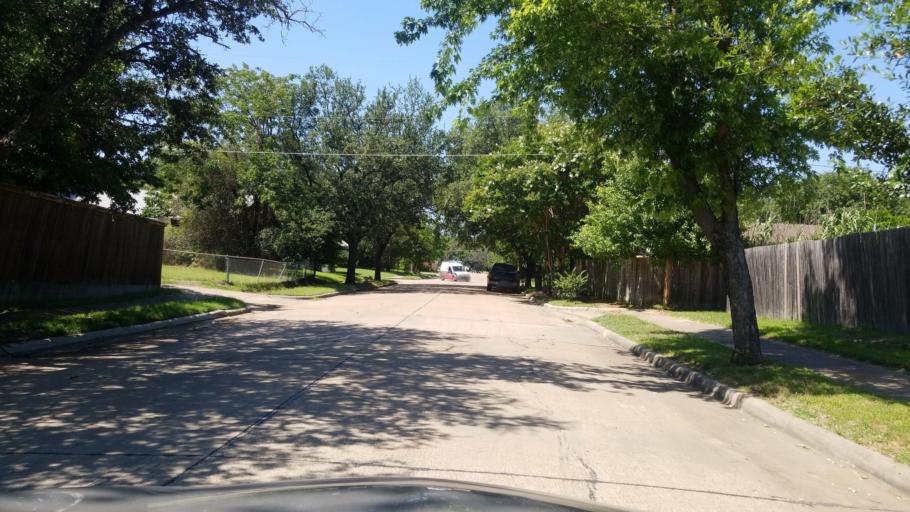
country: US
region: Texas
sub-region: Dallas County
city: Grand Prairie
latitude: 32.6925
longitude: -96.9990
